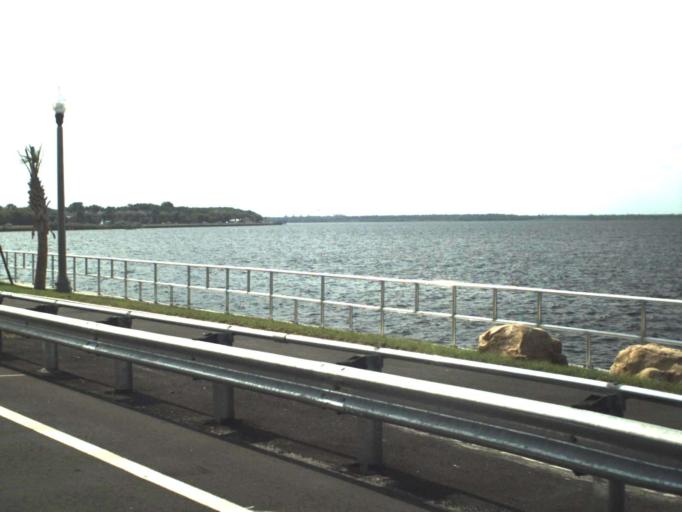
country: US
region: Florida
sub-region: Seminole County
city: Sanford
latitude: 28.8162
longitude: -81.2828
